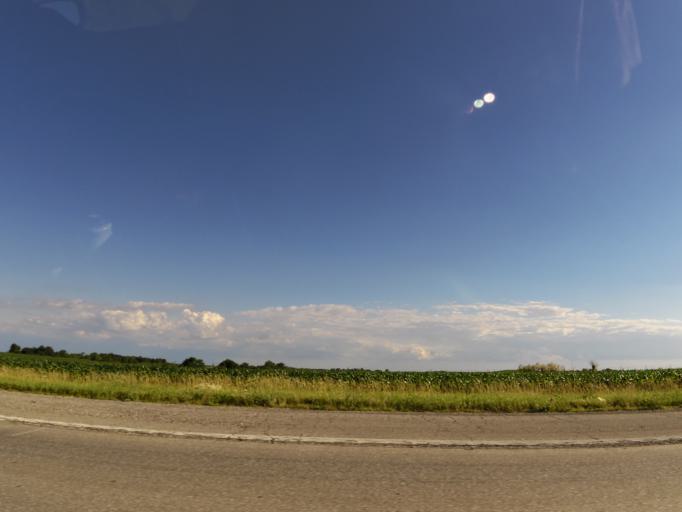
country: US
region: Missouri
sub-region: Pike County
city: Bowling Green
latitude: 39.3217
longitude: -91.1621
